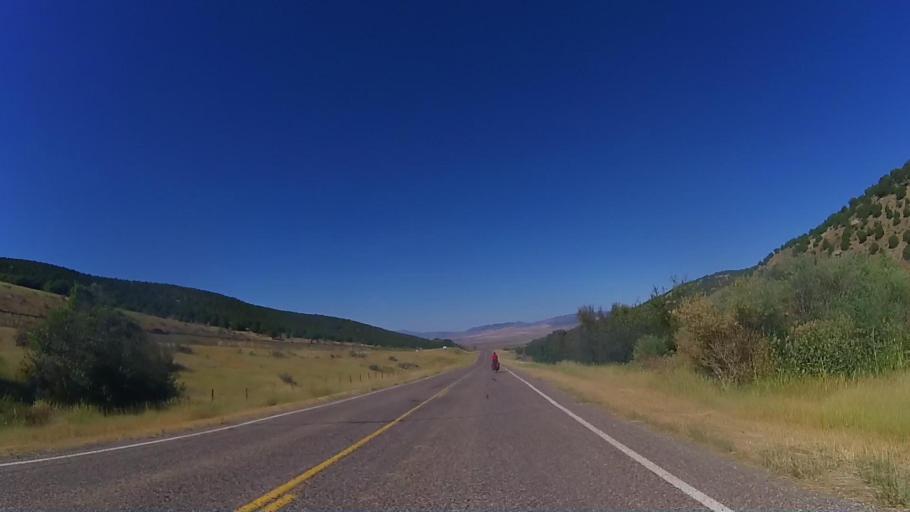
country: US
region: Idaho
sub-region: Oneida County
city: Malad City
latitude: 42.3537
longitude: -112.2221
